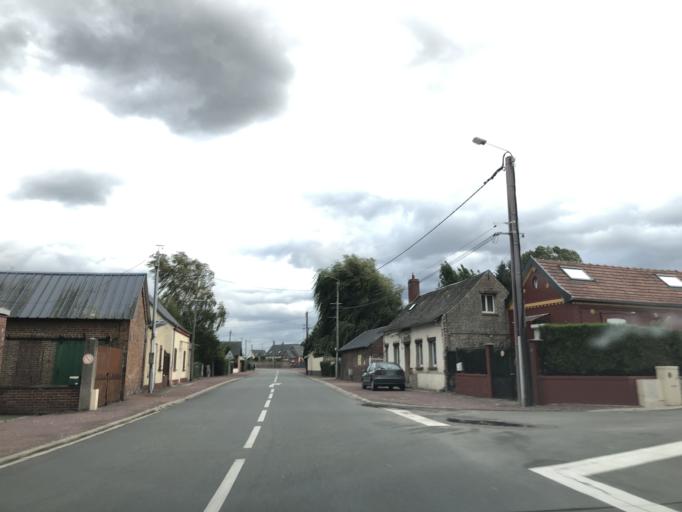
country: FR
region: Picardie
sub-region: Departement de la Somme
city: Pende
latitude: 50.1564
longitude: 1.5509
